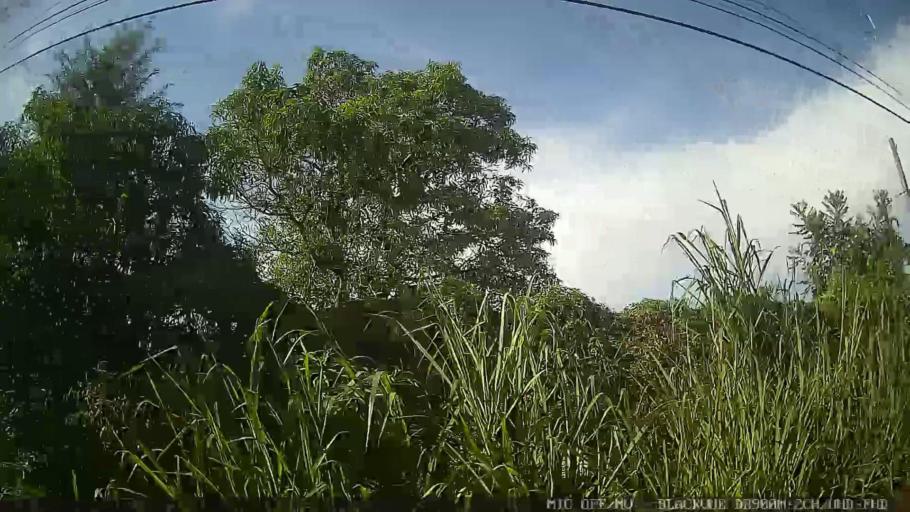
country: BR
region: Sao Paulo
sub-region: Tiete
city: Tiete
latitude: -23.0846
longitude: -47.6843
